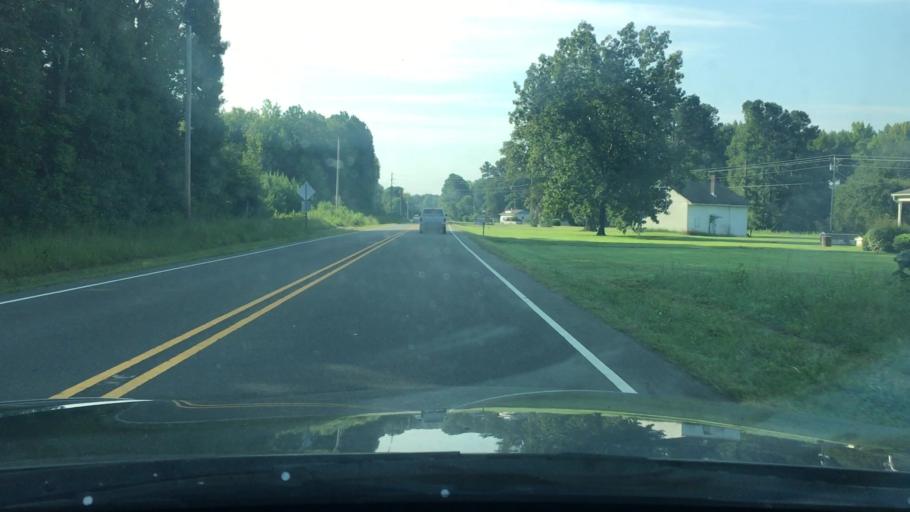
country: US
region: North Carolina
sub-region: Caswell County
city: Yanceyville
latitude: 36.2893
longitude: -79.3676
